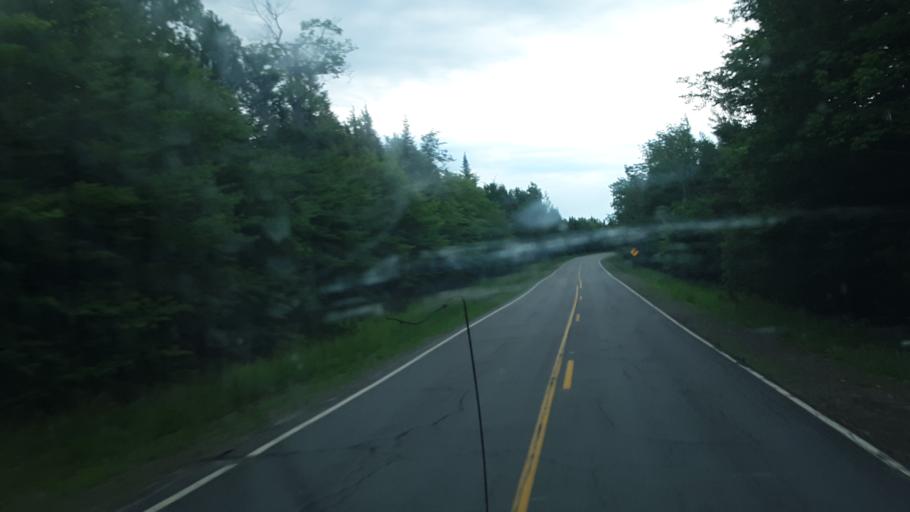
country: US
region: Maine
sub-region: Penobscot County
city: Medway
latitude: 45.7177
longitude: -68.2938
